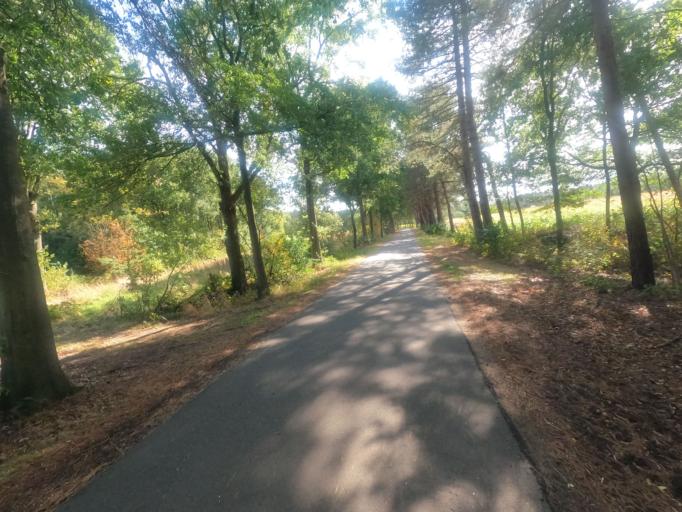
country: BE
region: Flanders
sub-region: Provincie Antwerpen
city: Lille
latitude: 51.2682
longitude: 4.8471
